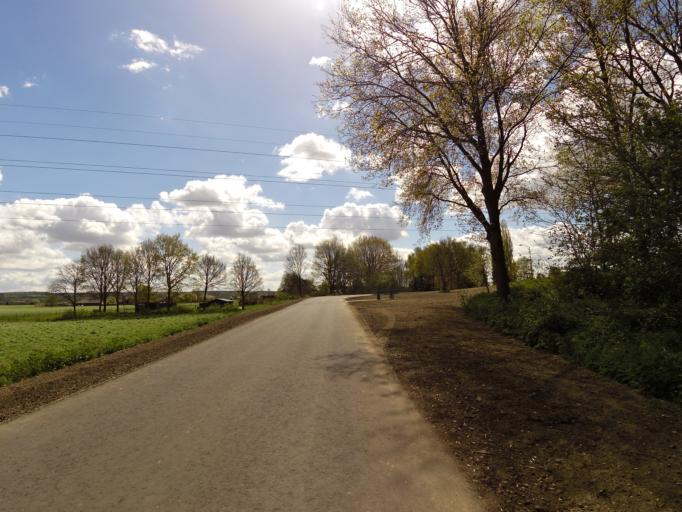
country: NL
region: Gelderland
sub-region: Gemeente Montferland
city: s-Heerenberg
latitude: 51.9425
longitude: 6.2028
